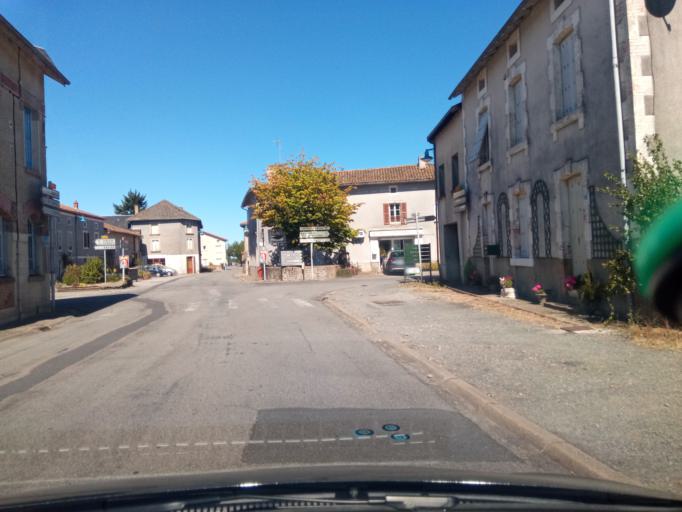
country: FR
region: Limousin
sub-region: Departement de la Haute-Vienne
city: Nantiat
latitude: 46.0774
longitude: 1.2012
